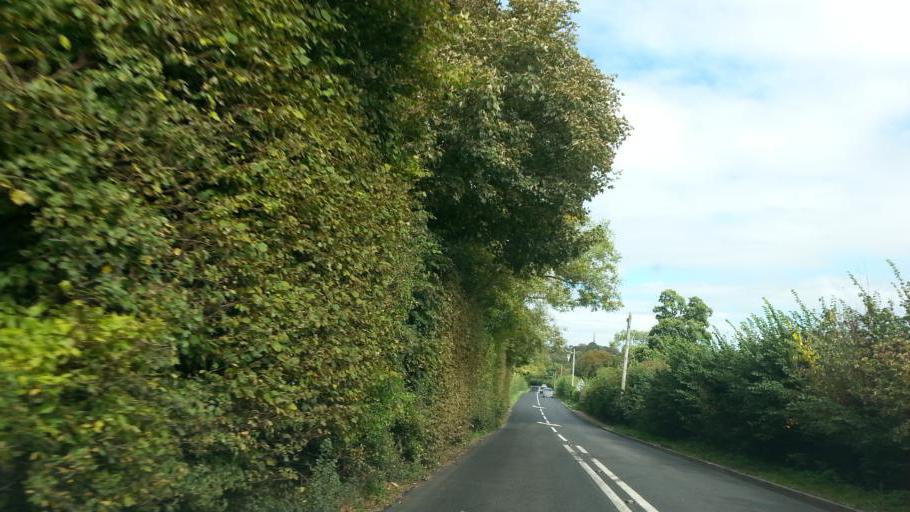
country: GB
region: England
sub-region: Gloucestershire
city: Painswick
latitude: 51.7756
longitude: -2.2102
